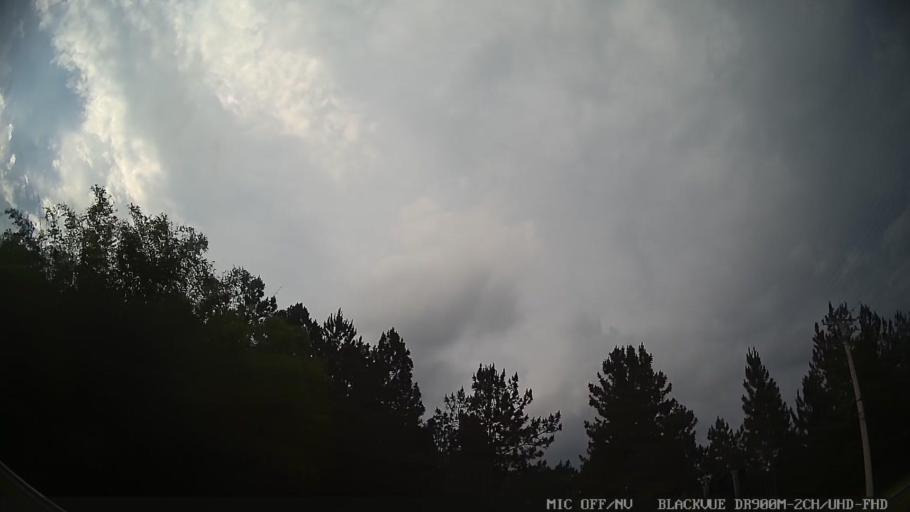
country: BR
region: Sao Paulo
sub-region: Itatiba
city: Itatiba
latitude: -23.0476
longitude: -46.8651
